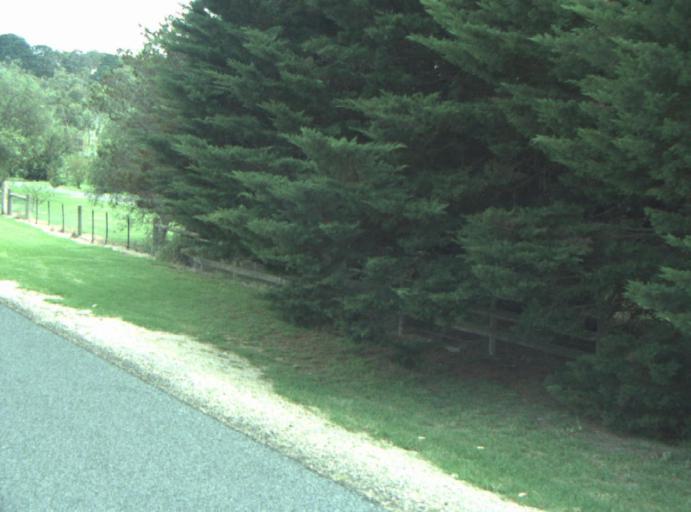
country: AU
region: Victoria
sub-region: Greater Geelong
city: Wandana Heights
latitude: -38.2070
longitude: 144.2935
